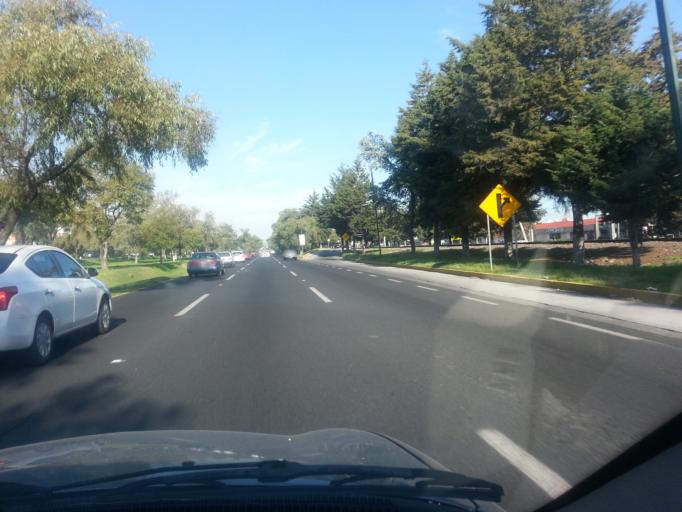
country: MX
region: Mexico
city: Santa Maria Totoltepec
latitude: 19.2873
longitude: -99.5858
